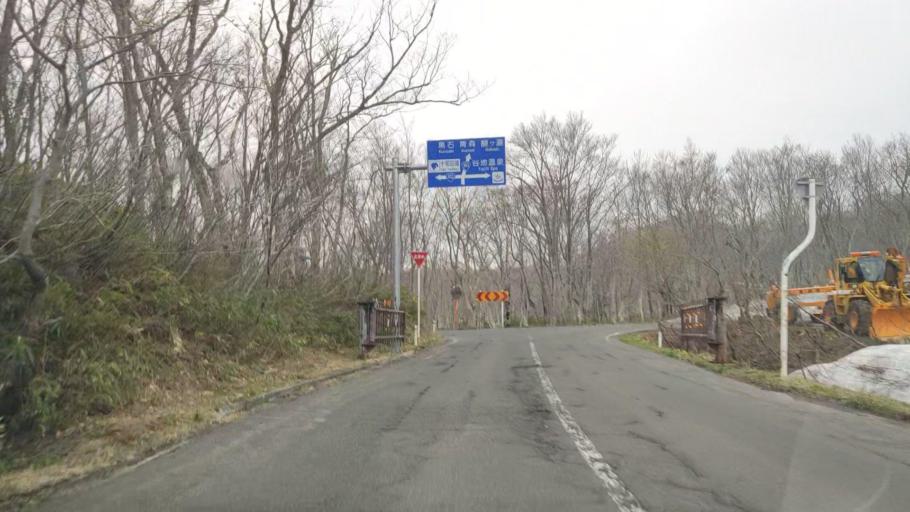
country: JP
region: Aomori
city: Aomori Shi
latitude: 40.6314
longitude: 140.9294
